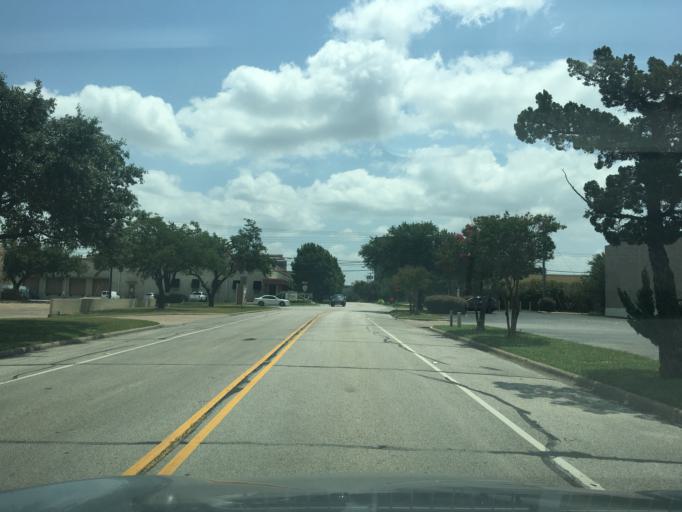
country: US
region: Texas
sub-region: Dallas County
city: Addison
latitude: 32.9289
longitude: -96.8338
